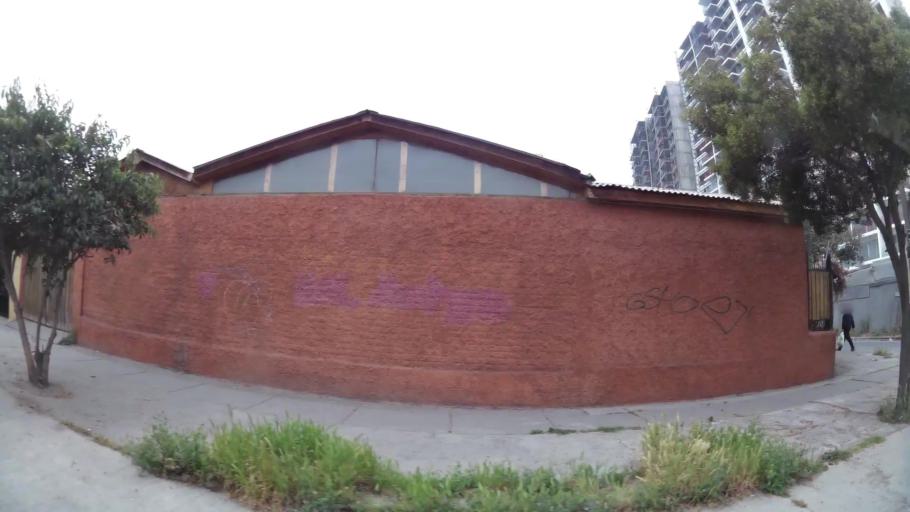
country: CL
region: Santiago Metropolitan
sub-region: Provincia de Santiago
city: Villa Presidente Frei, Nunoa, Santiago, Chile
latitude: -33.5135
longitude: -70.5942
